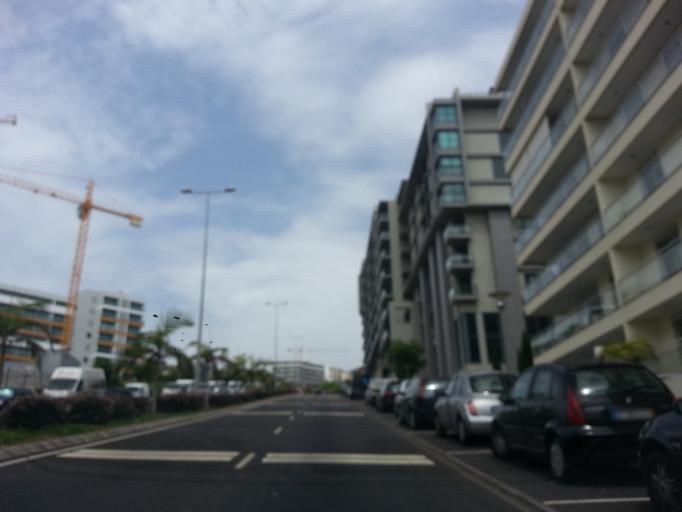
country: PT
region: Madeira
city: Camara de Lobos
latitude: 32.6420
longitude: -16.9471
